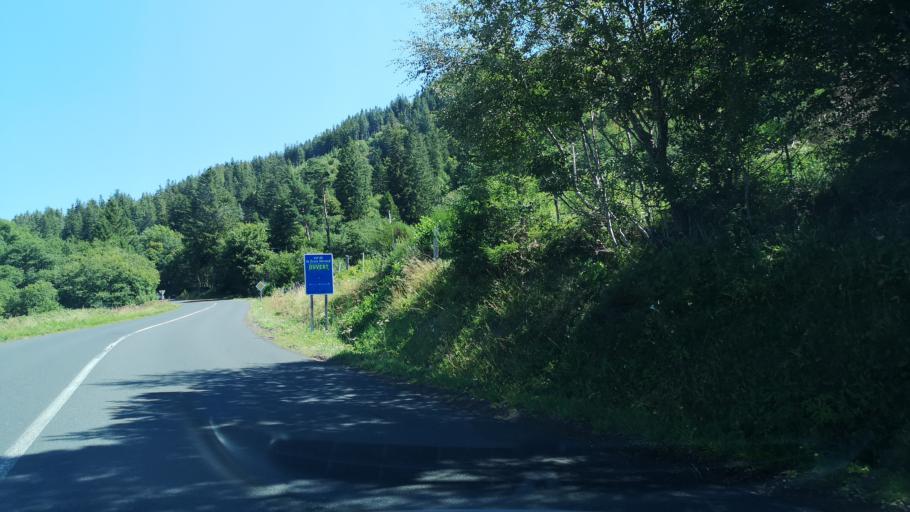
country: FR
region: Auvergne
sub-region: Departement du Puy-de-Dome
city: Mont-Dore
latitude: 45.5856
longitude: 2.8219
